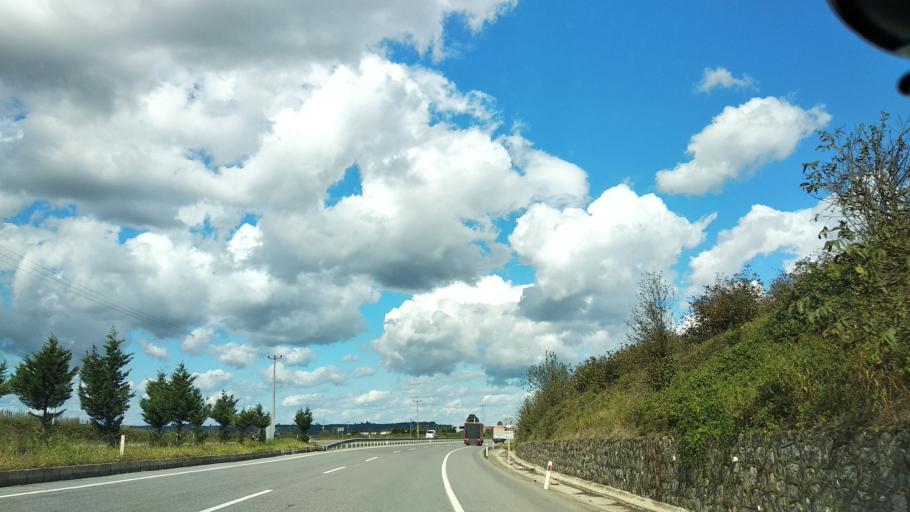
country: TR
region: Sakarya
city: Ferizli
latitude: 40.9703
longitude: 30.5081
